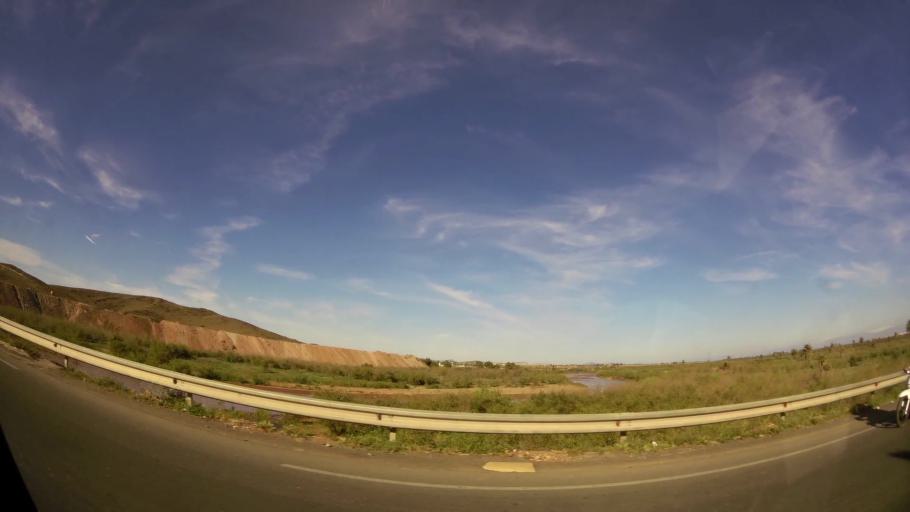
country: MA
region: Marrakech-Tensift-Al Haouz
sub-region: Marrakech
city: Marrakesh
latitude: 31.7002
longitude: -8.0606
